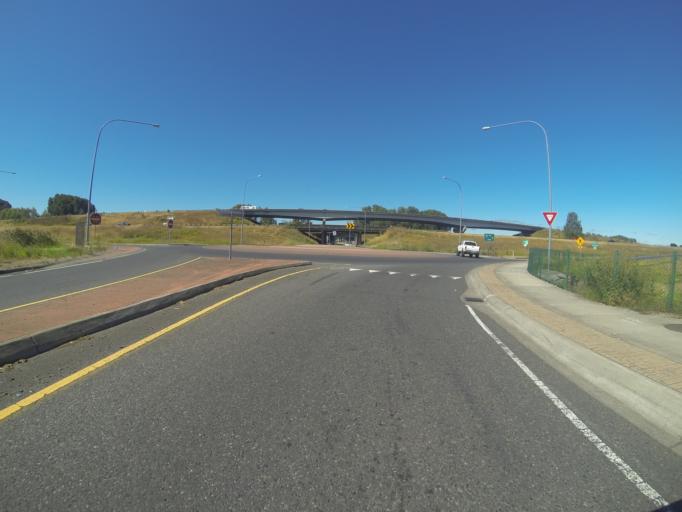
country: US
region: Washington
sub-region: Cowlitz County
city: Woodland
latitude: 45.9280
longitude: -122.7549
